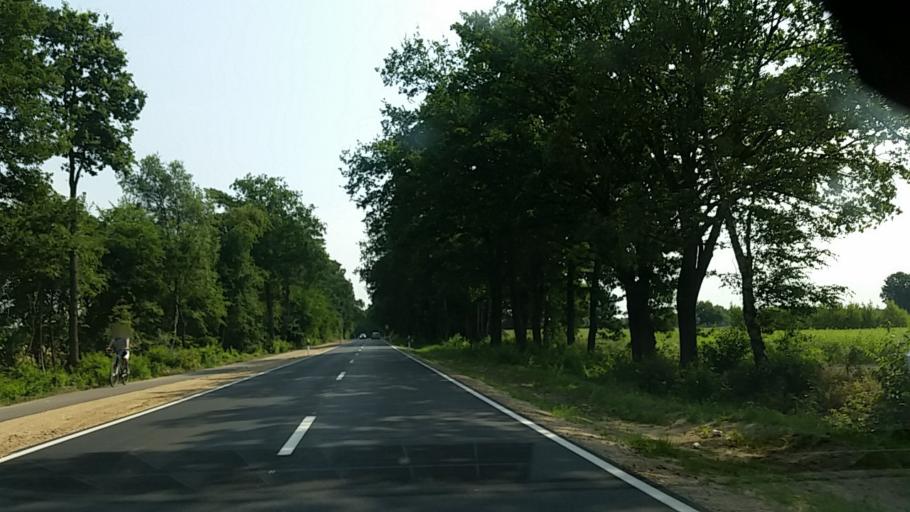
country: DE
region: Schleswig-Holstein
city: Rausdorf
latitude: 53.5624
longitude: 10.2961
